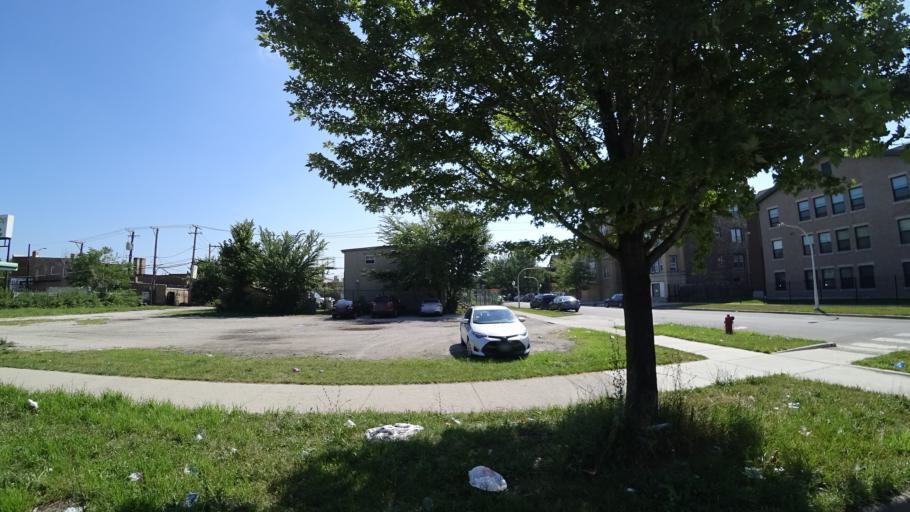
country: US
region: Illinois
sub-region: Cook County
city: Cicero
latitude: 41.8728
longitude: -87.7197
